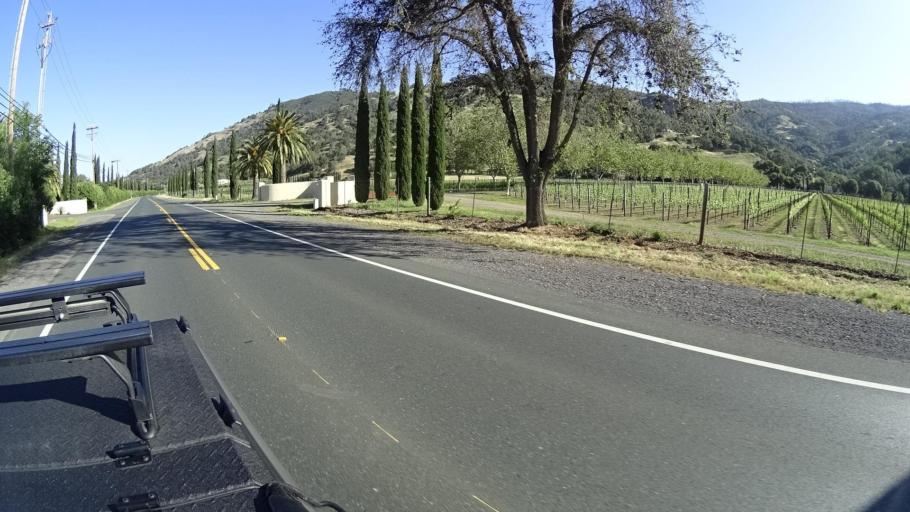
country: US
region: California
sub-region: Lake County
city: Lucerne
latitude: 39.1082
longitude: -122.8157
